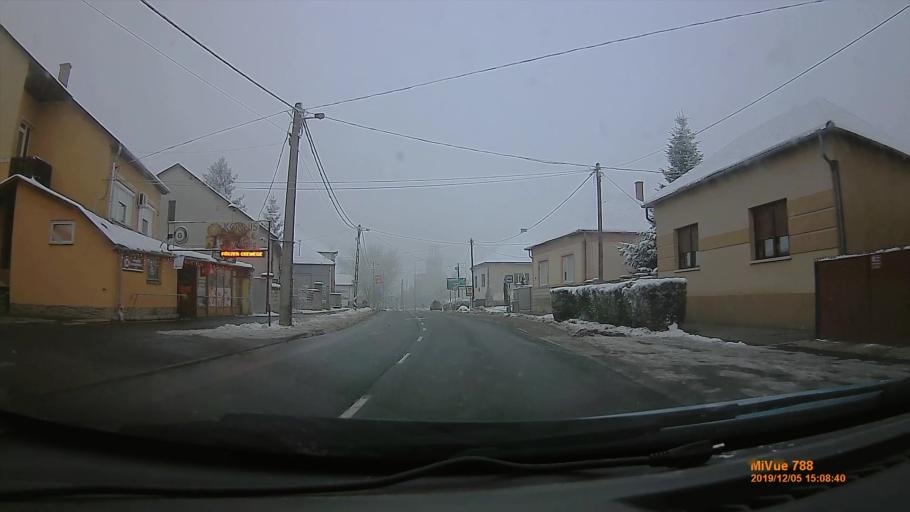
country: HU
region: Szabolcs-Szatmar-Bereg
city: Rakamaz
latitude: 48.1233
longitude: 21.4596
